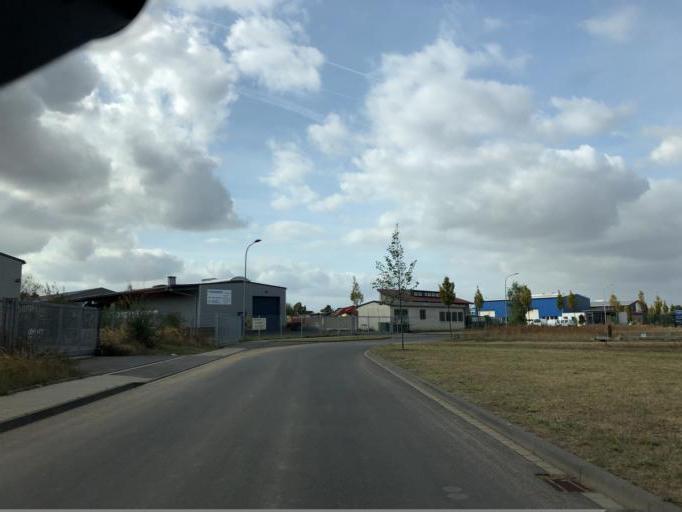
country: DE
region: North Rhine-Westphalia
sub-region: Regierungsbezirk Koln
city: Rheinbach
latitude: 50.6530
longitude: 6.8793
